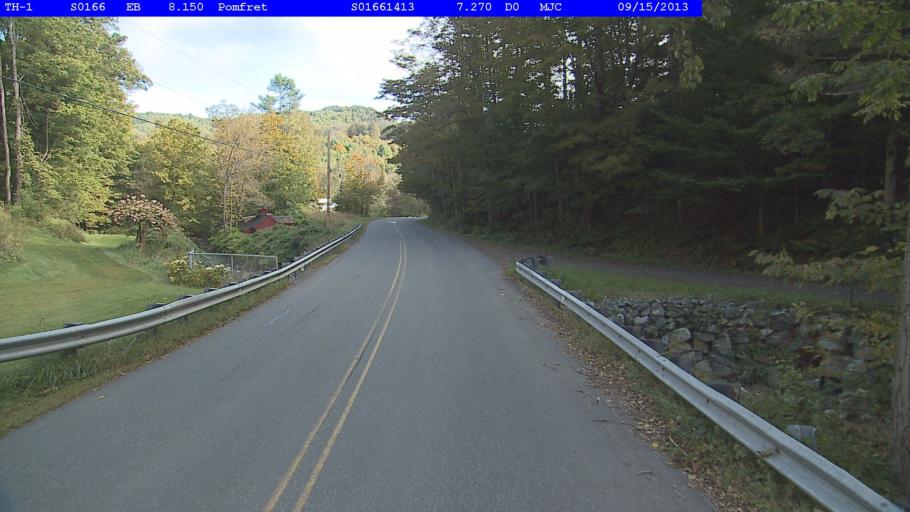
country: US
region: Vermont
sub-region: Windsor County
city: Woodstock
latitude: 43.7249
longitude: -72.4770
